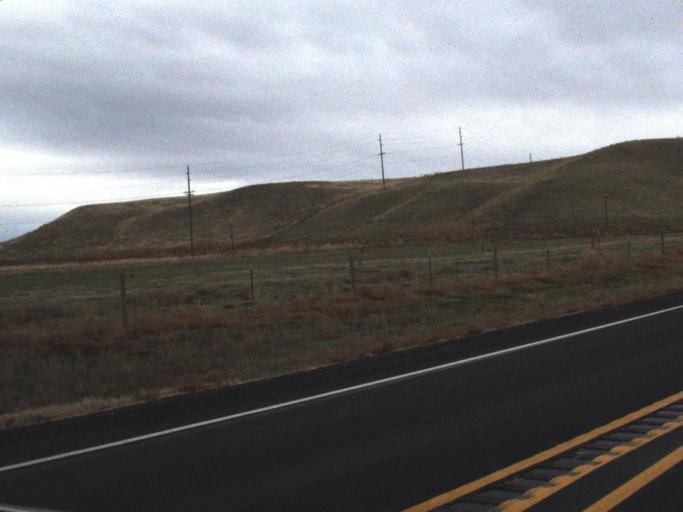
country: US
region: Washington
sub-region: Walla Walla County
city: Garrett
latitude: 46.0535
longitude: -118.6056
